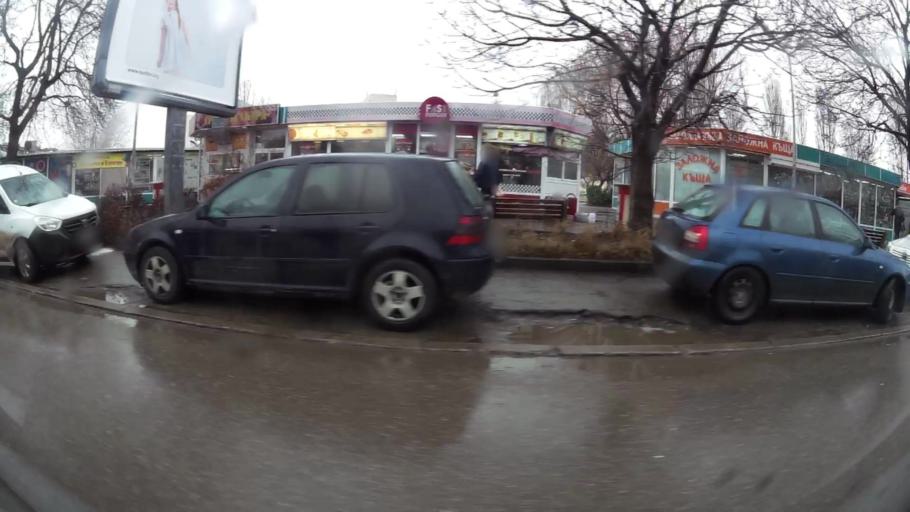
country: BG
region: Sofia-Capital
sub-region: Stolichna Obshtina
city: Sofia
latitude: 42.6673
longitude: 23.3963
